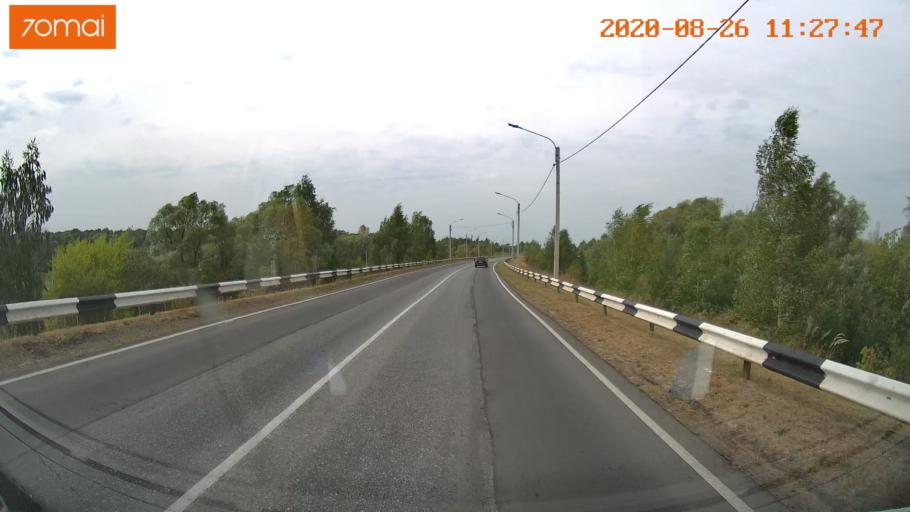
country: RU
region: Rjazan
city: Shilovo
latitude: 54.3246
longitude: 40.9291
